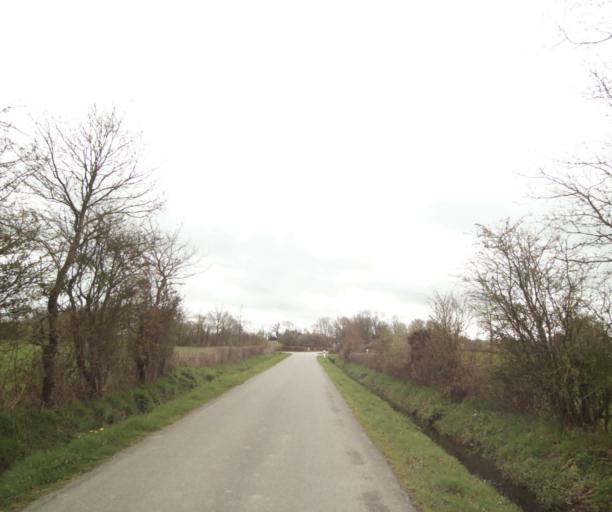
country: FR
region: Pays de la Loire
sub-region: Departement de la Loire-Atlantique
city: Bouvron
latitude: 47.4385
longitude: -1.8605
